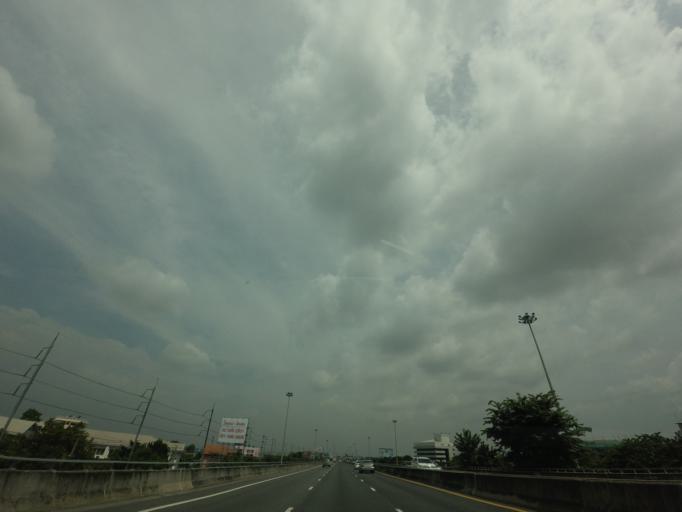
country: TH
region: Bangkok
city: Wang Thonglang
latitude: 13.7938
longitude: 100.6120
